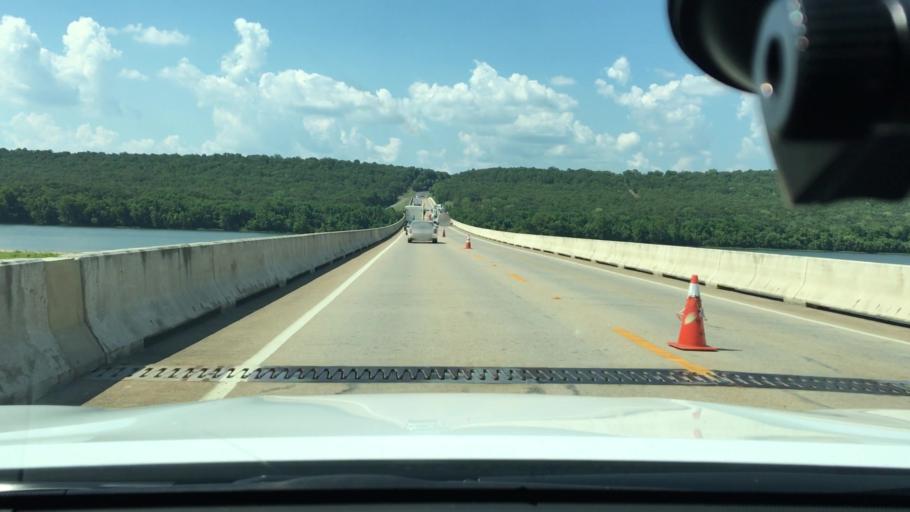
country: US
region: Arkansas
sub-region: Johnson County
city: Clarksville
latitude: 35.4063
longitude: -93.5316
